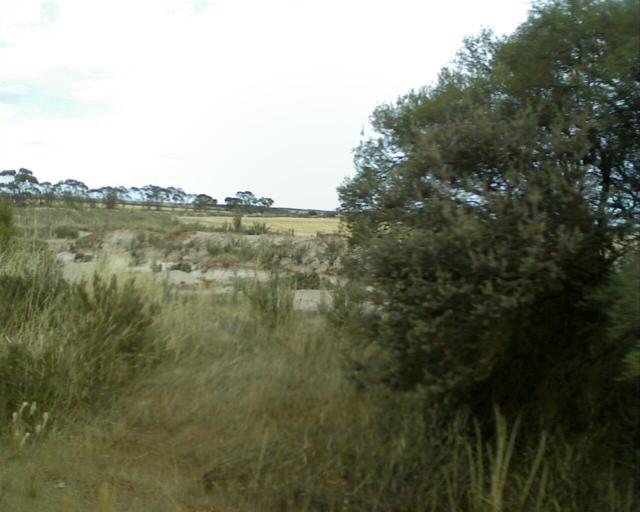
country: AU
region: Western Australia
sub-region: Moora
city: Moora
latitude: -29.7639
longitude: 116.0267
